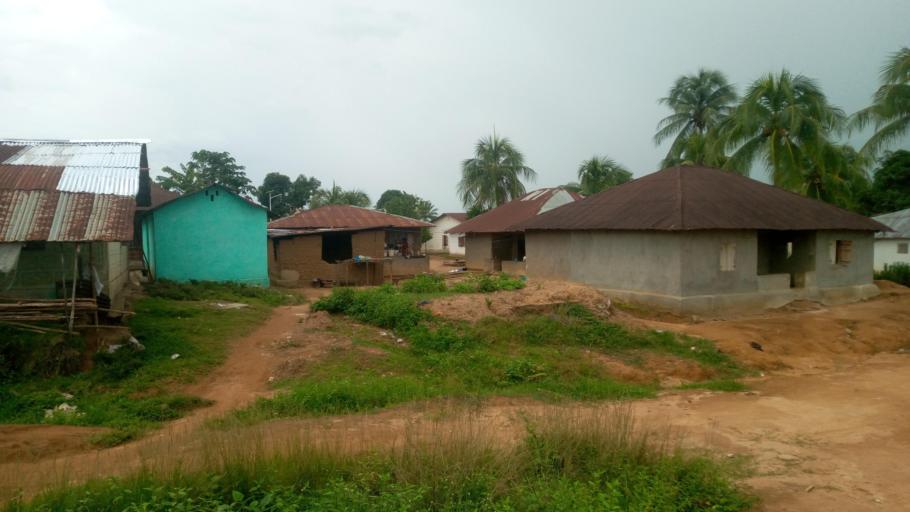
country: SL
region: Southern Province
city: Mogbwemo
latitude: 7.6067
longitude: -12.1700
